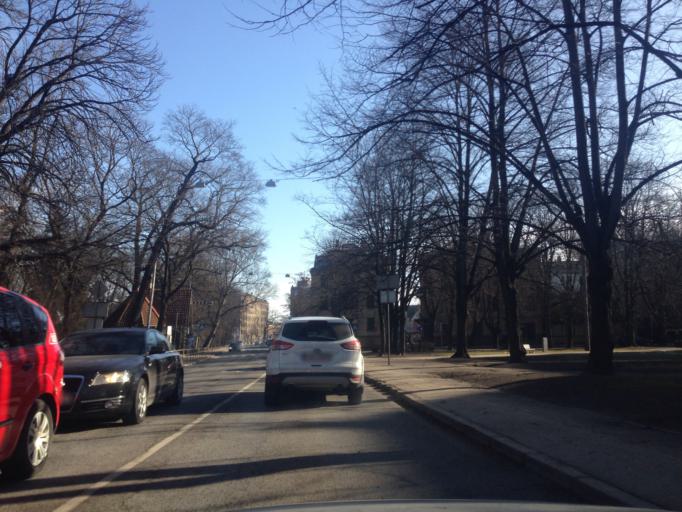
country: LV
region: Riga
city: Riga
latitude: 56.9625
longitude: 24.0988
